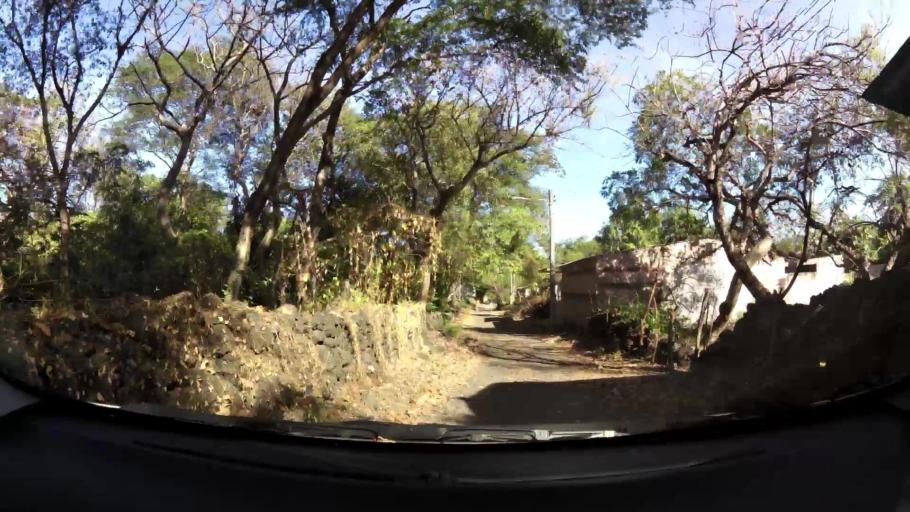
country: SV
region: San Miguel
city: San Miguel
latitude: 13.4664
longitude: -88.2009
